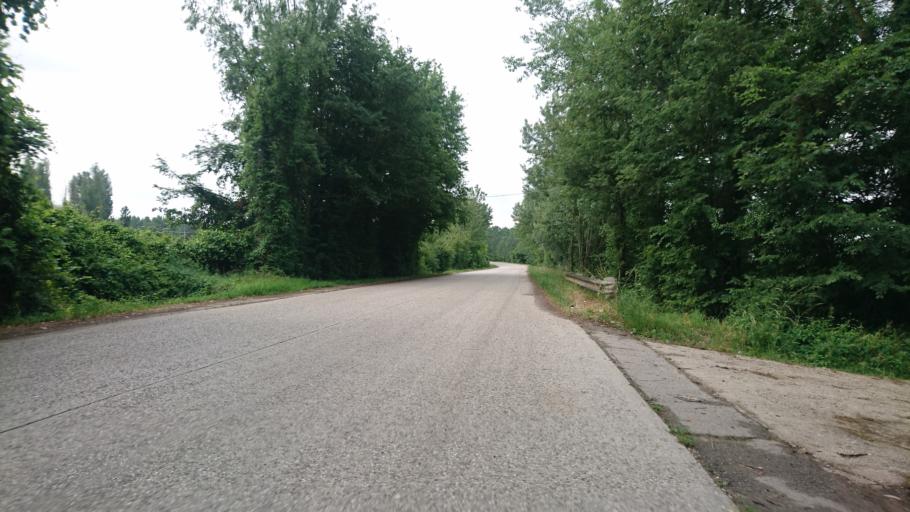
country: IT
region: Veneto
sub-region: Provincia di Padova
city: Monselice
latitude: 45.2324
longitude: 11.7213
